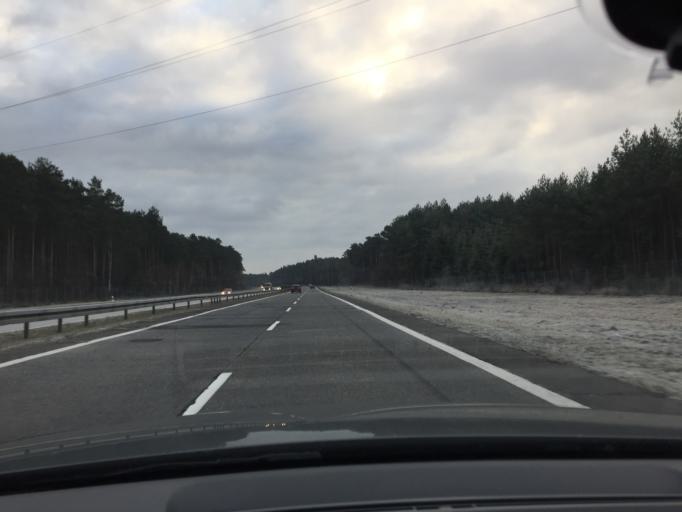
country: PL
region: Lubusz
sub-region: Powiat zarski
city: Lipinki Luzyckie
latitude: 51.6160
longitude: 14.9201
